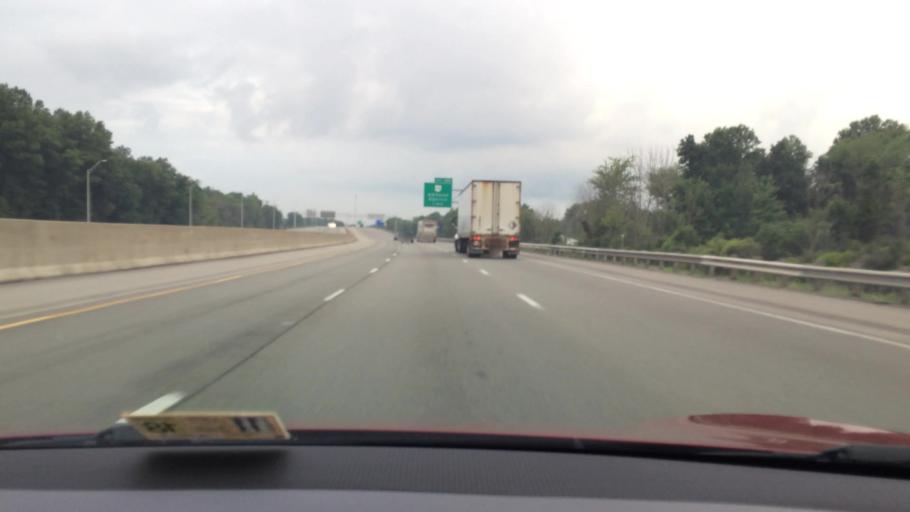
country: US
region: Ohio
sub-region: Lorain County
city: Amherst
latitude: 41.3883
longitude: -82.1733
